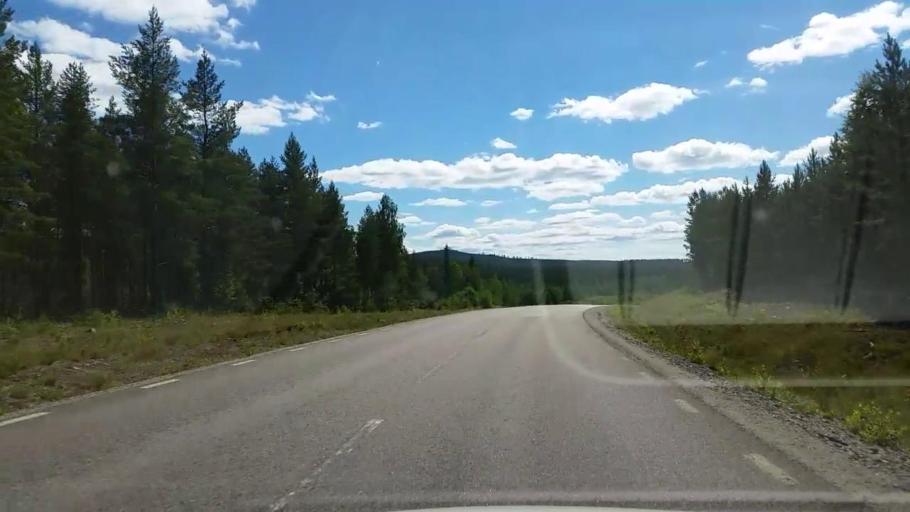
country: SE
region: Dalarna
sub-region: Faluns Kommun
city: Svardsjo
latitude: 61.0163
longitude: 15.7554
